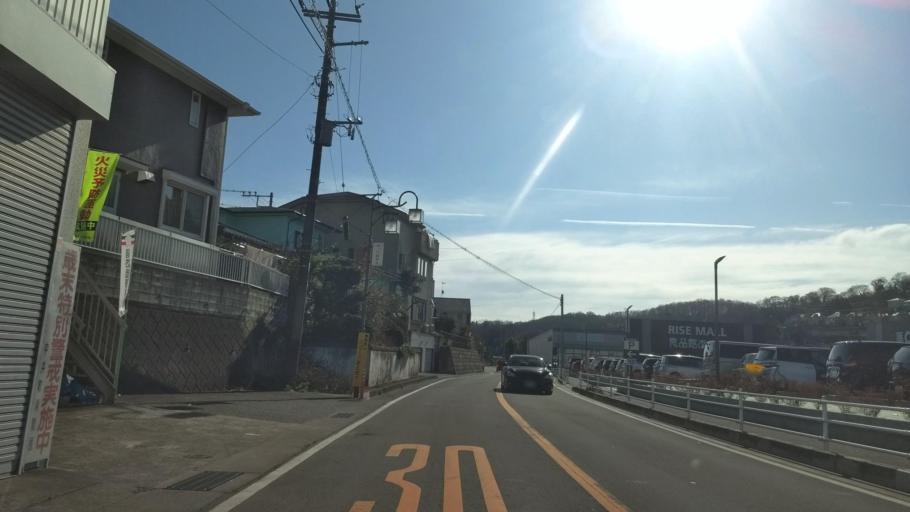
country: JP
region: Kanagawa
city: Hadano
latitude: 35.3380
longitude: 139.2327
